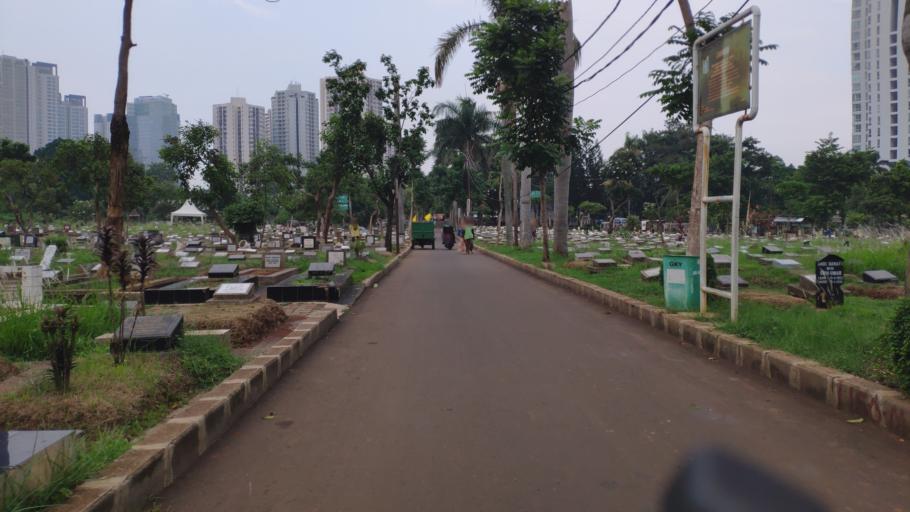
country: ID
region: Jakarta Raya
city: Jakarta
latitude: -6.2243
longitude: 106.8369
